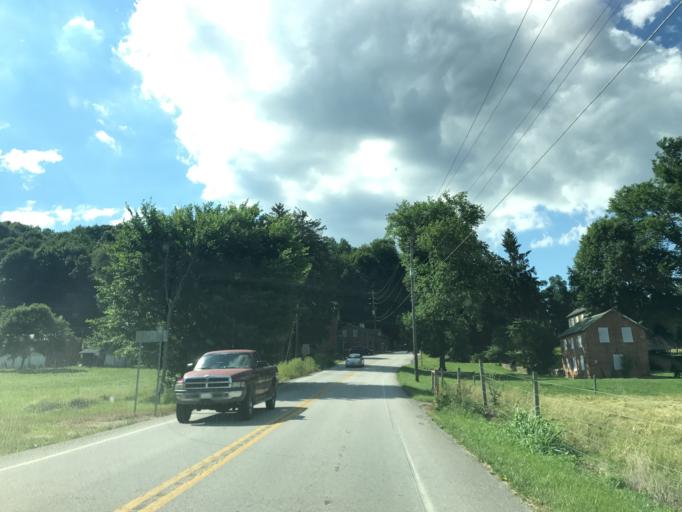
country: US
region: Pennsylvania
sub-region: York County
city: Glen Rock
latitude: 39.7468
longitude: -76.8035
